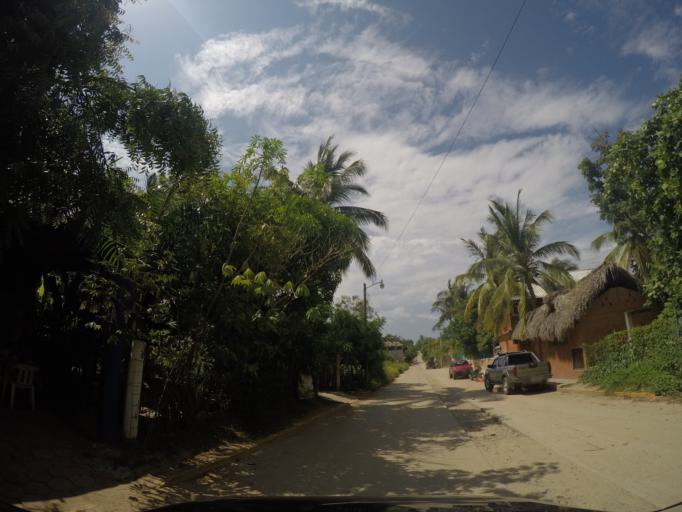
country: MX
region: Oaxaca
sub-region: Santa Maria Colotepec
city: Brisas de Zicatela
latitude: 15.8348
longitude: -97.0424
